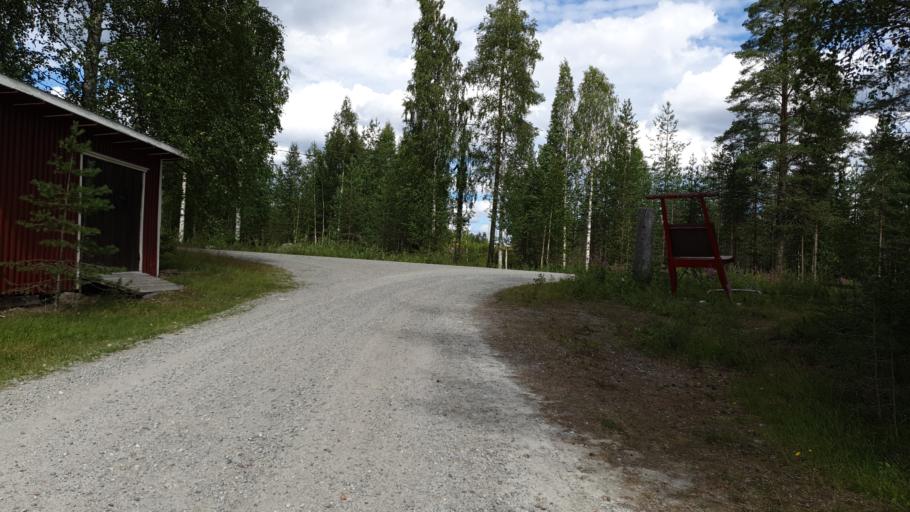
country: FI
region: Kainuu
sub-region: Kehys-Kainuu
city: Kuhmo
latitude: 64.3820
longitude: 29.7818
